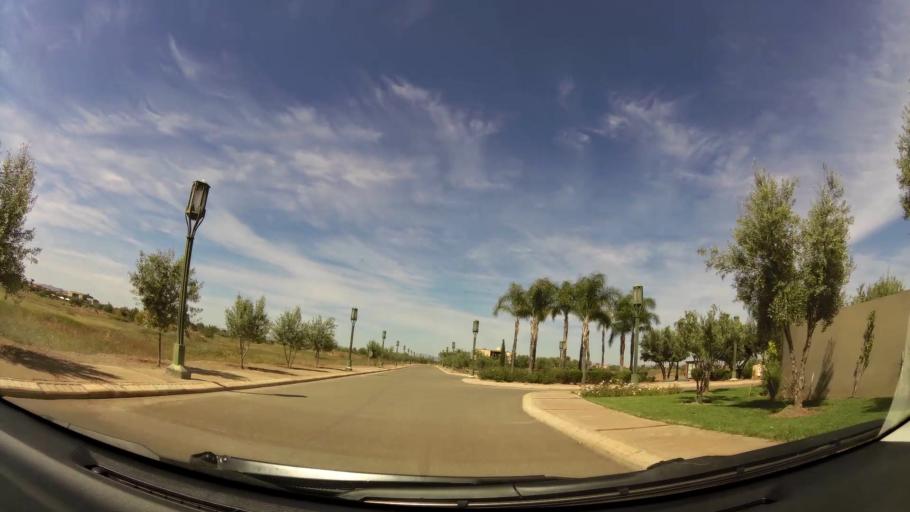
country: MA
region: Marrakech-Tensift-Al Haouz
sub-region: Marrakech
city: Marrakesh
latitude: 31.6141
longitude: -7.9295
